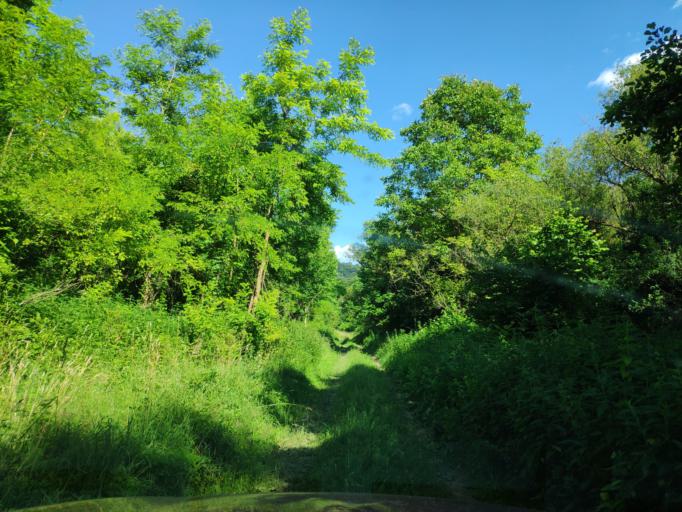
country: SK
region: Banskobystricky
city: Rimavska Sobota
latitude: 48.2562
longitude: 20.1195
